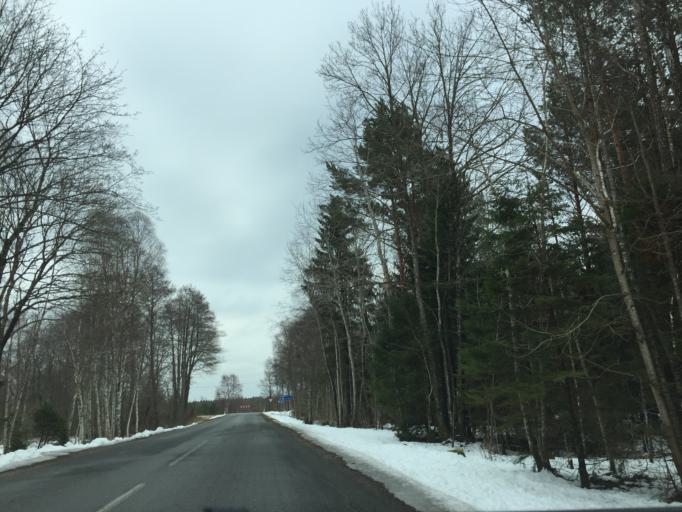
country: EE
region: Saare
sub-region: Kuressaare linn
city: Kuressaare
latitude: 58.4179
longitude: 22.1285
